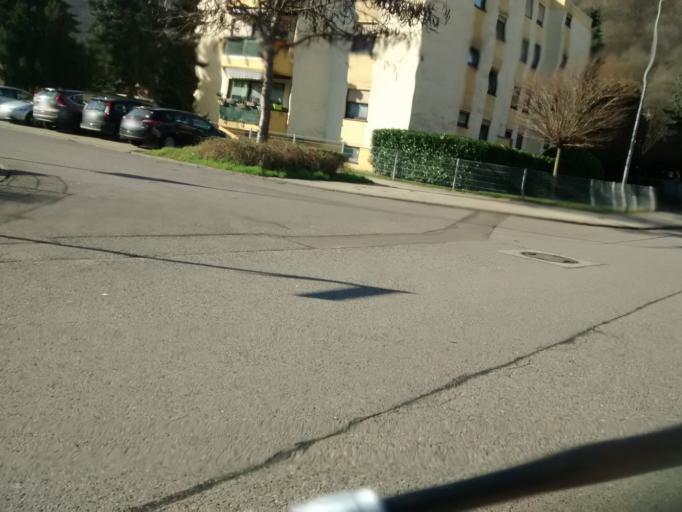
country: DE
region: Rheinland-Pfalz
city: Kenn
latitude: 49.8158
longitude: 6.6991
